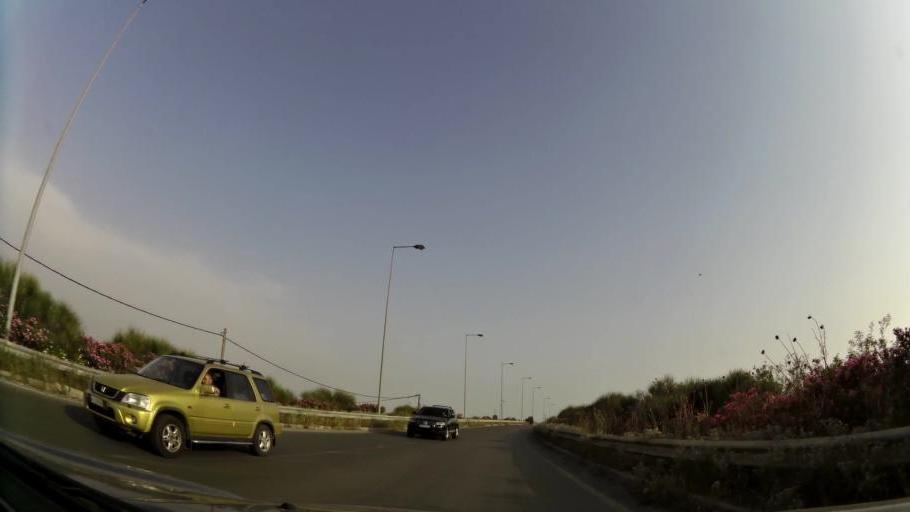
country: GR
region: Central Macedonia
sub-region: Nomos Thessalonikis
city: Evosmos
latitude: 40.6971
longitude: 22.9095
